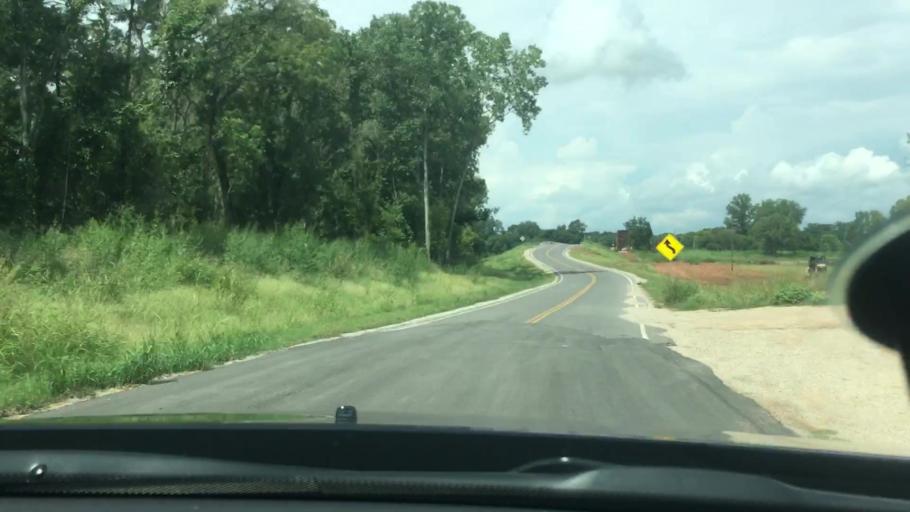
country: US
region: Oklahoma
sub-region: Carter County
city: Dickson
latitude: 34.2273
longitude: -96.9044
